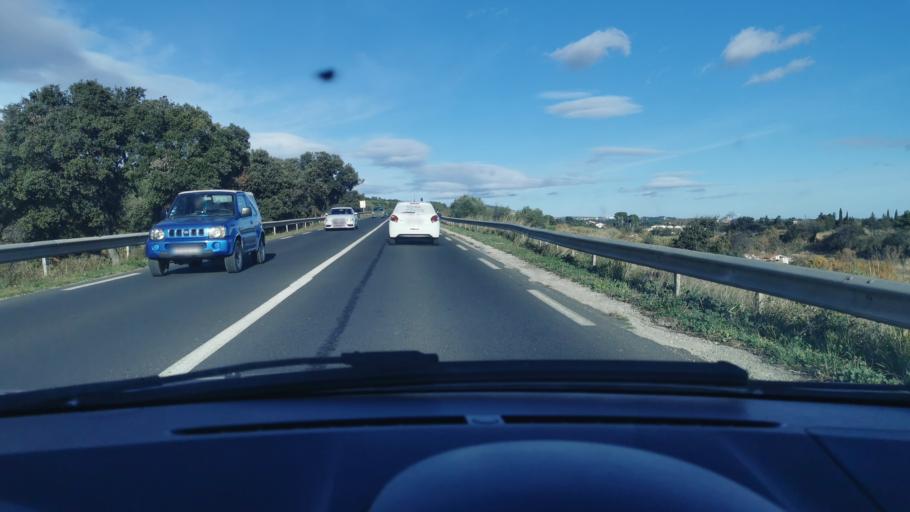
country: FR
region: Languedoc-Roussillon
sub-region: Departement de l'Herault
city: Vic-la-Gardiole
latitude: 43.4927
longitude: 3.7751
